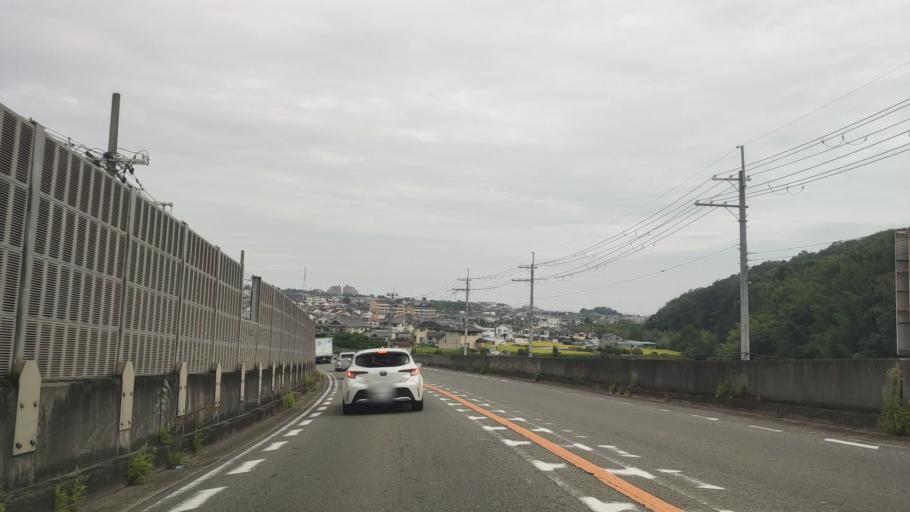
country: JP
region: Osaka
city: Tondabayashicho
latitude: 34.4404
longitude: 135.5590
